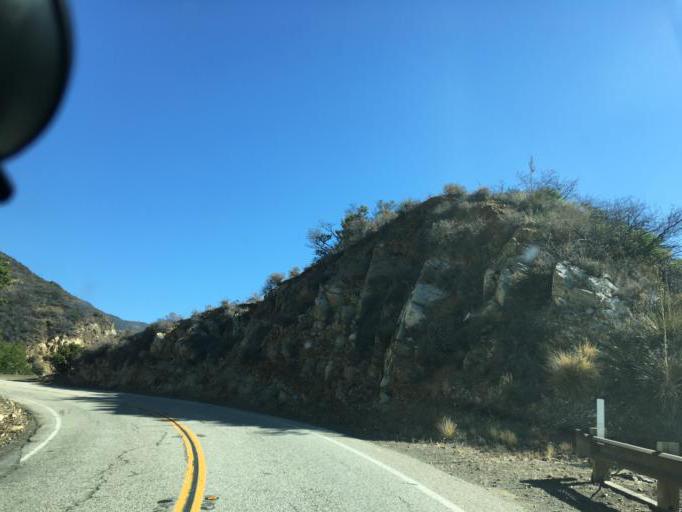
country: US
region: California
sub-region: Ventura County
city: Casa Conejo
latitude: 34.0579
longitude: -118.9344
